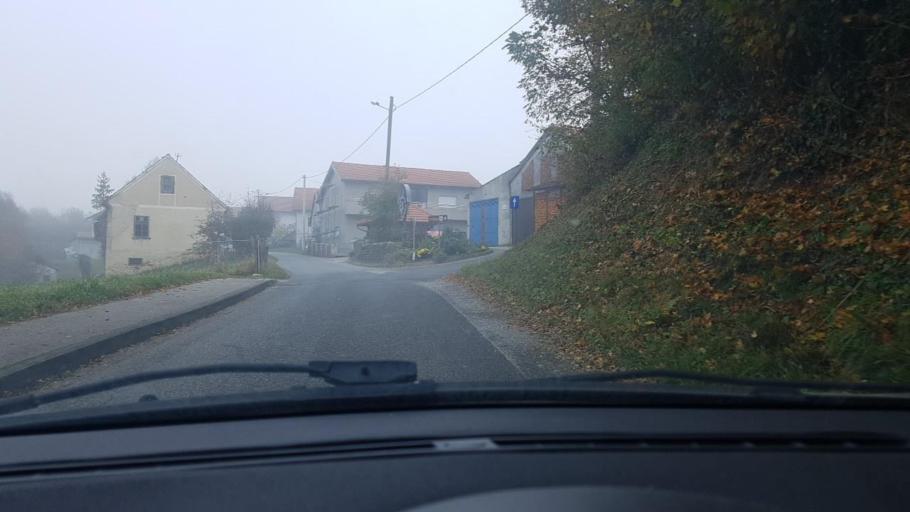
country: HR
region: Krapinsko-Zagorska
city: Mihovljan
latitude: 46.1344
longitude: 15.9740
